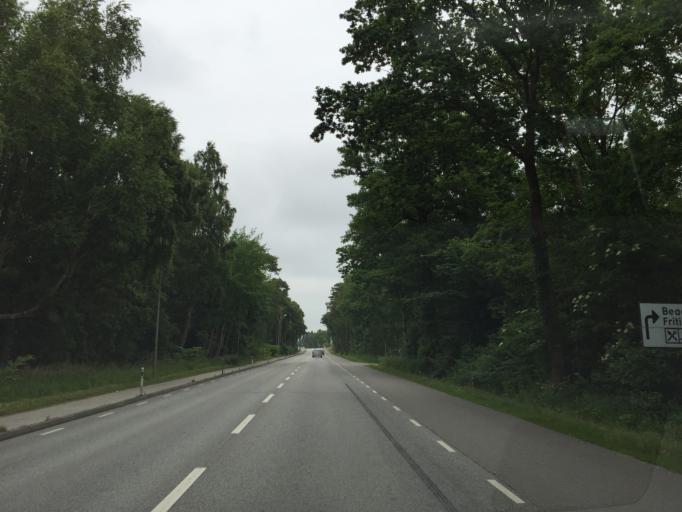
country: SE
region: Skane
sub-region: Ystads Kommun
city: Ystad
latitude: 55.4319
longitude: 13.8596
